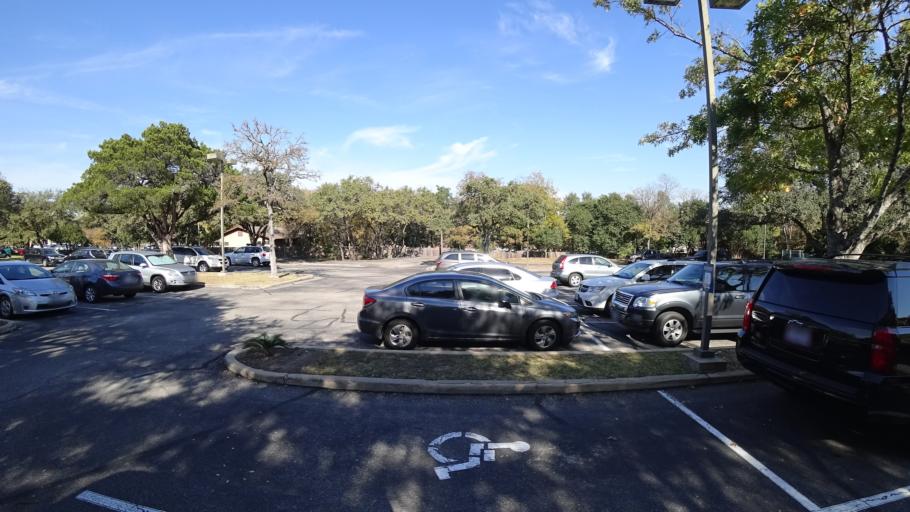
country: US
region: Texas
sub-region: Williamson County
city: Jollyville
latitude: 30.3695
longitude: -97.7575
